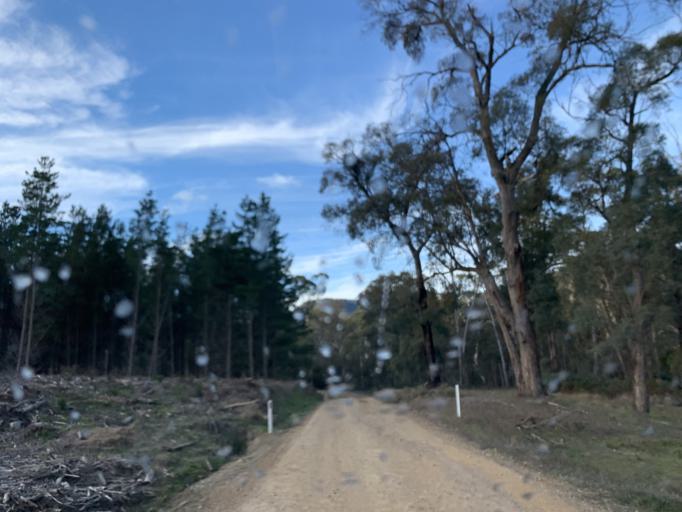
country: AU
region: Victoria
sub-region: Mansfield
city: Mansfield
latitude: -36.9260
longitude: 146.0979
